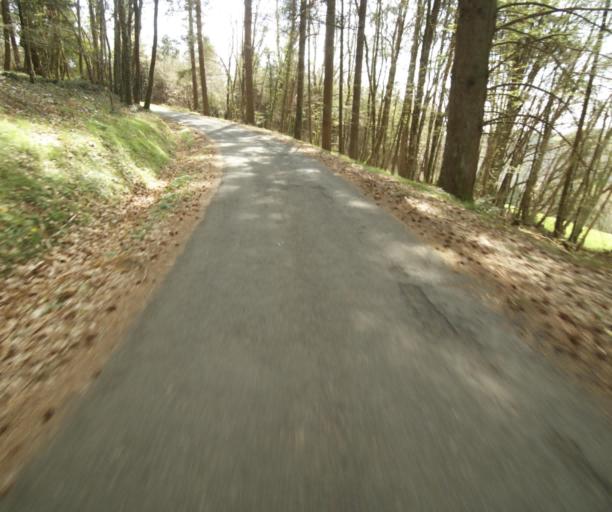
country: FR
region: Limousin
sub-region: Departement de la Correze
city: Naves
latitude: 45.3651
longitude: 1.7921
